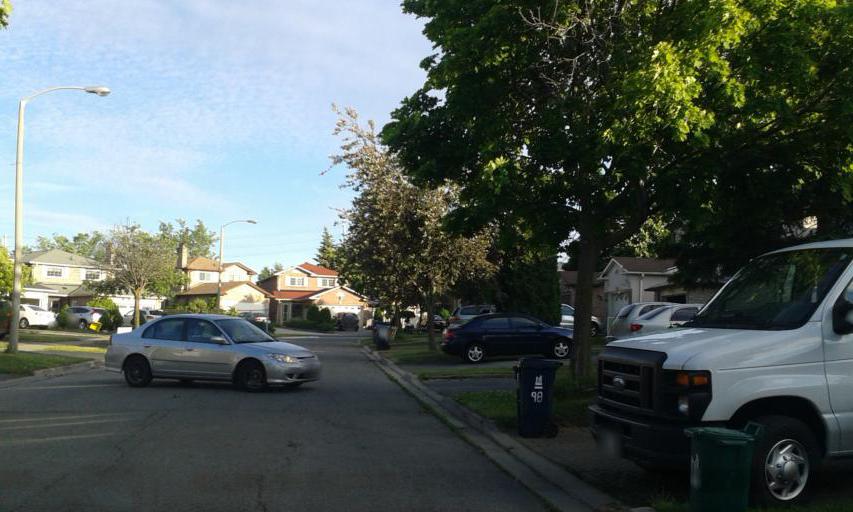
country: CA
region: Ontario
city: Scarborough
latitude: 43.8111
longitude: -79.2590
